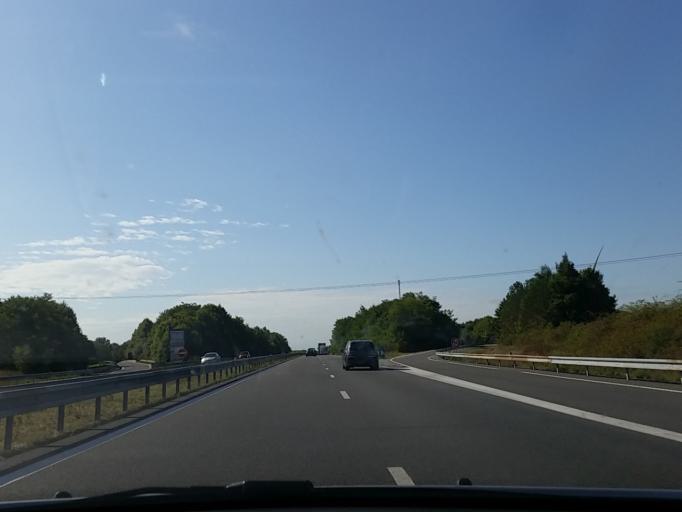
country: FR
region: Centre
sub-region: Departement du Cher
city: Mehun-sur-Yevre
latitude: 47.1483
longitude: 2.1849
